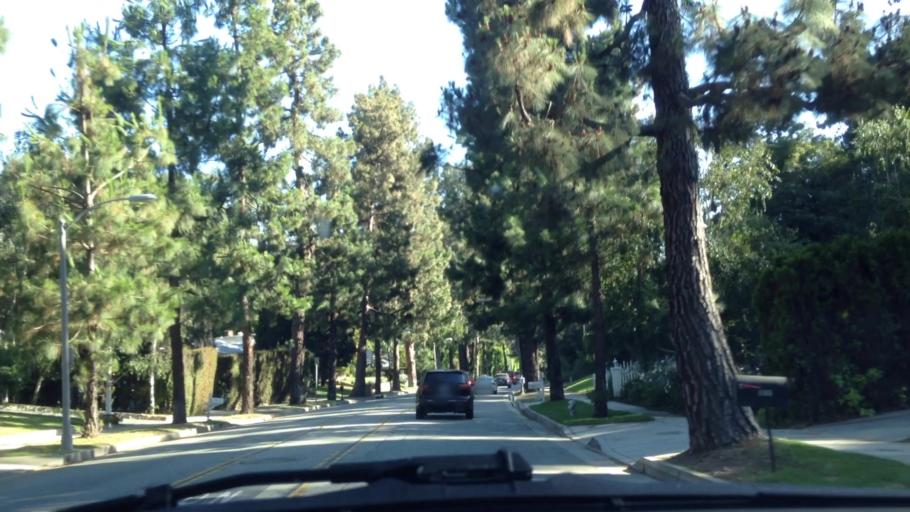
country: US
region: California
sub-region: Los Angeles County
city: Beverly Hills
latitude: 34.0952
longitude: -118.4067
